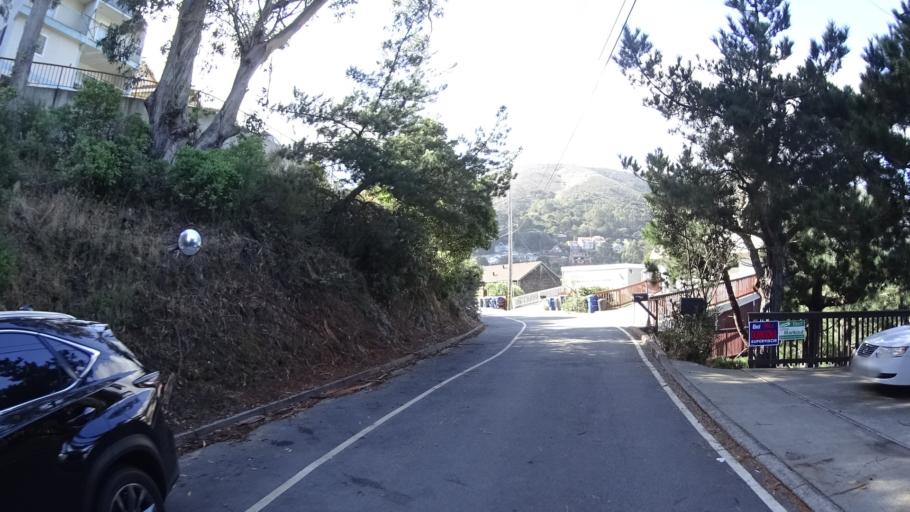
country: US
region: California
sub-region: San Mateo County
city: Brisbane
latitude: 37.6820
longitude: -122.3977
